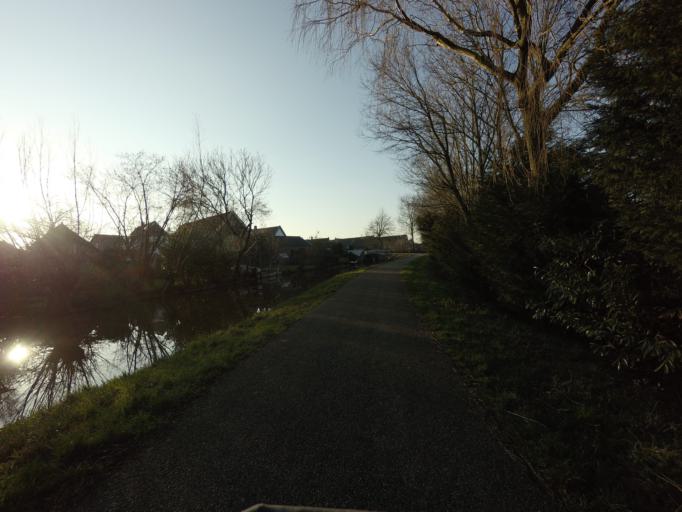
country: NL
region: South Holland
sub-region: Gemeente Gorinchem
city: Gorinchem
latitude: 51.8832
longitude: 4.9464
